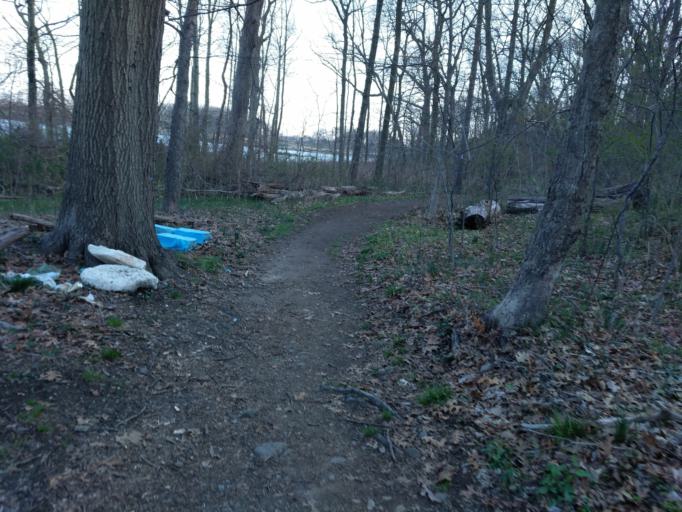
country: US
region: New York
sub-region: Westchester County
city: Pelham Manor
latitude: 40.8766
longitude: -73.7858
